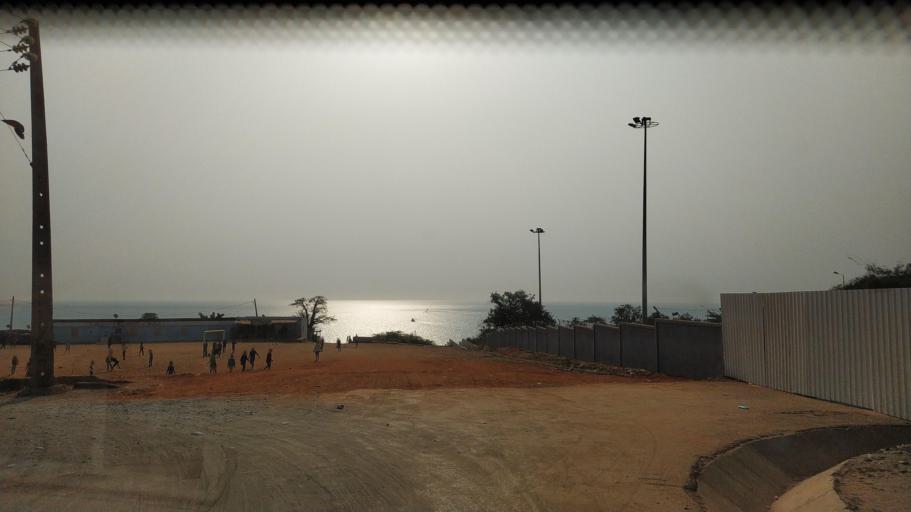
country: AO
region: Luanda
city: Luanda
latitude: -8.8658
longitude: 13.2034
